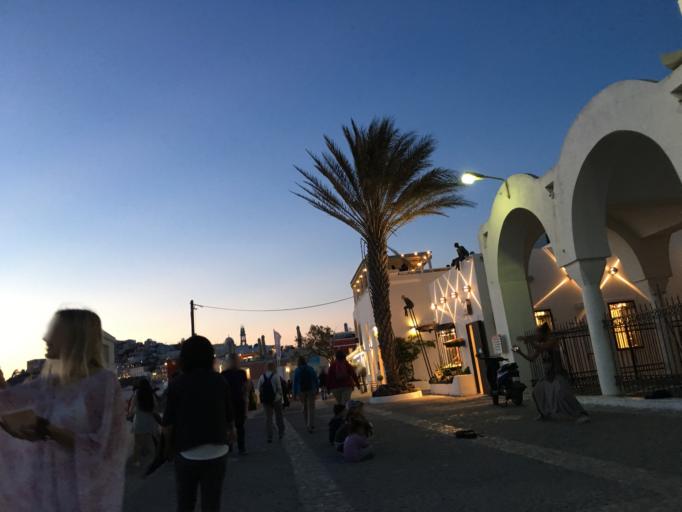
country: GR
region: South Aegean
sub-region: Nomos Kykladon
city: Fira
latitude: 36.4169
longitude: 25.4316
